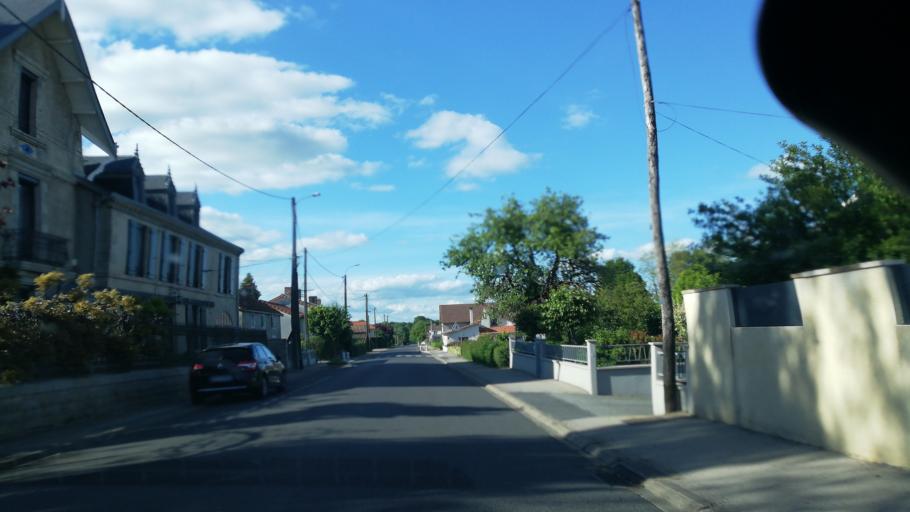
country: FR
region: Poitou-Charentes
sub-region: Departement des Deux-Sevres
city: La Chapelle-Saint-Laurent
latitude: 46.7516
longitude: -0.4748
